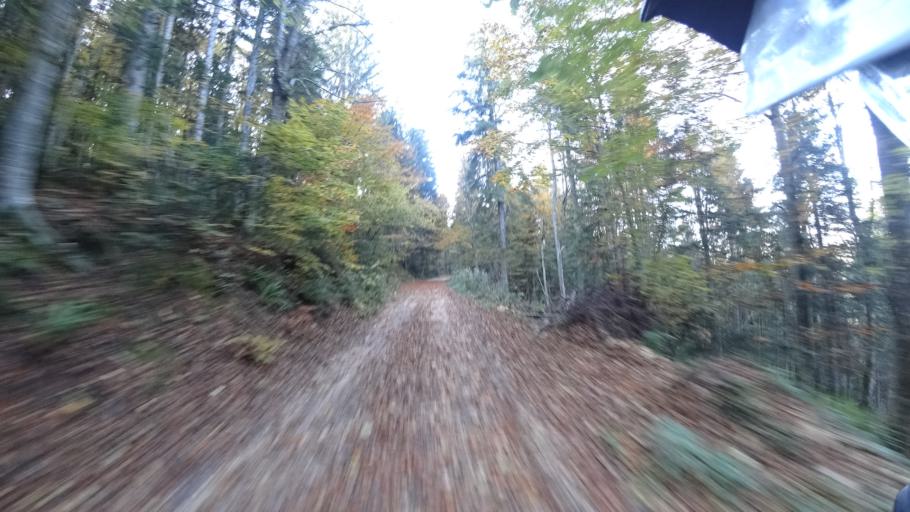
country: HR
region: Licko-Senjska
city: Jezerce
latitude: 44.9303
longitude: 15.4609
